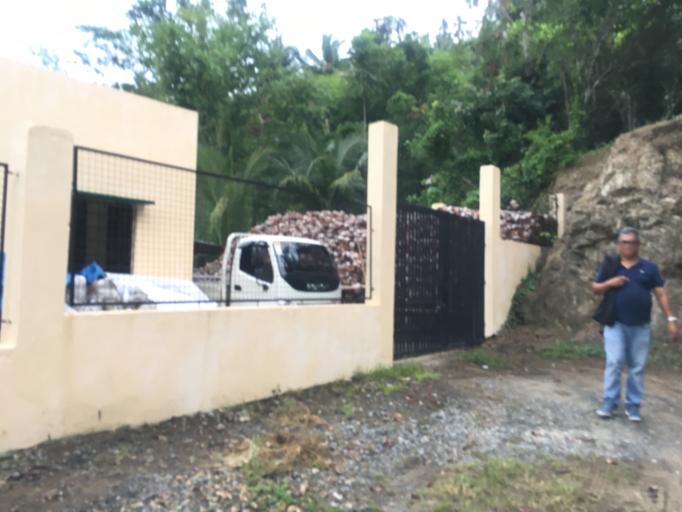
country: PH
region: Western Visayas
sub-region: Province of Aklan
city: Lupo
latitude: 11.4989
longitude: 122.4824
